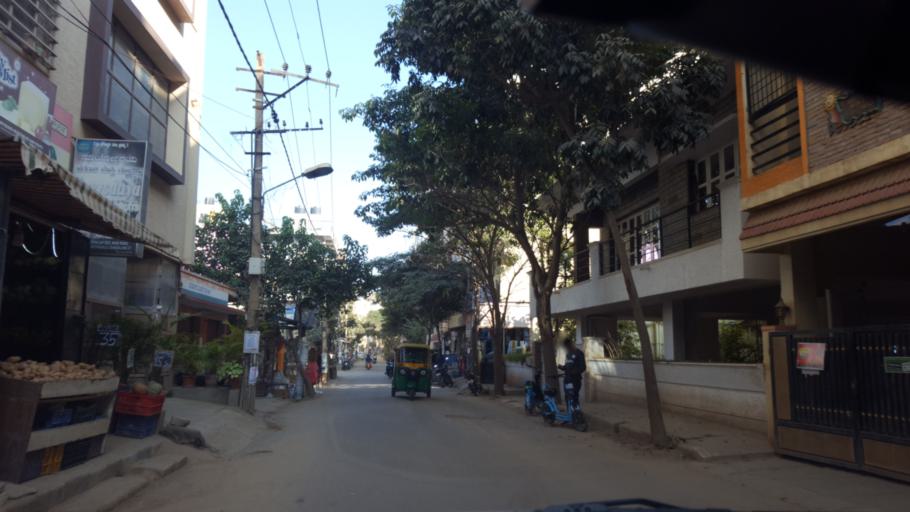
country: IN
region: Karnataka
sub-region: Bangalore Urban
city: Bangalore
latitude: 12.9499
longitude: 77.7119
